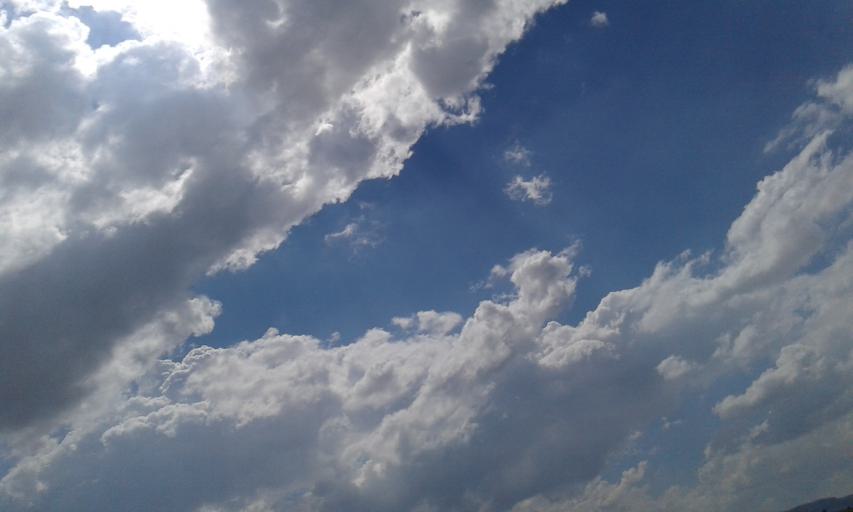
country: LS
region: Maseru
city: Maseru
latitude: -29.4140
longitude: 27.5704
